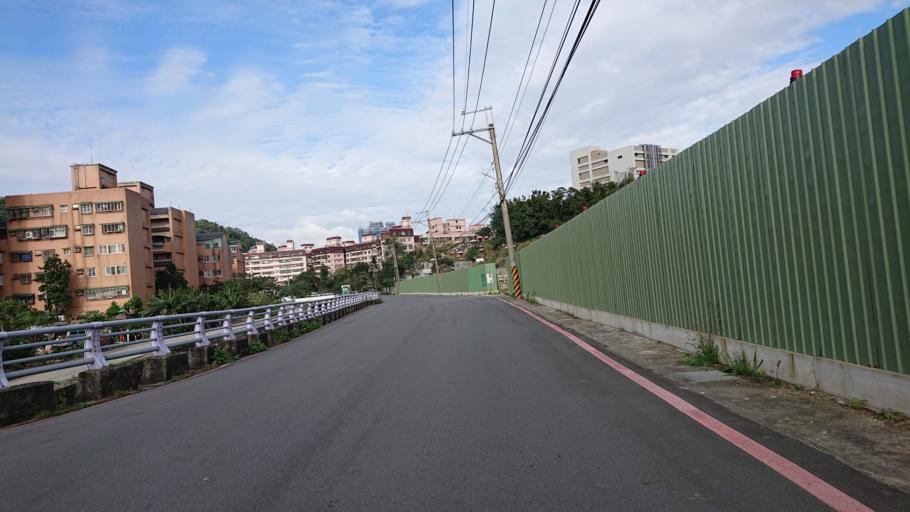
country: TW
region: Taiwan
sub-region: Taoyuan
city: Taoyuan
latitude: 24.9234
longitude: 121.3634
